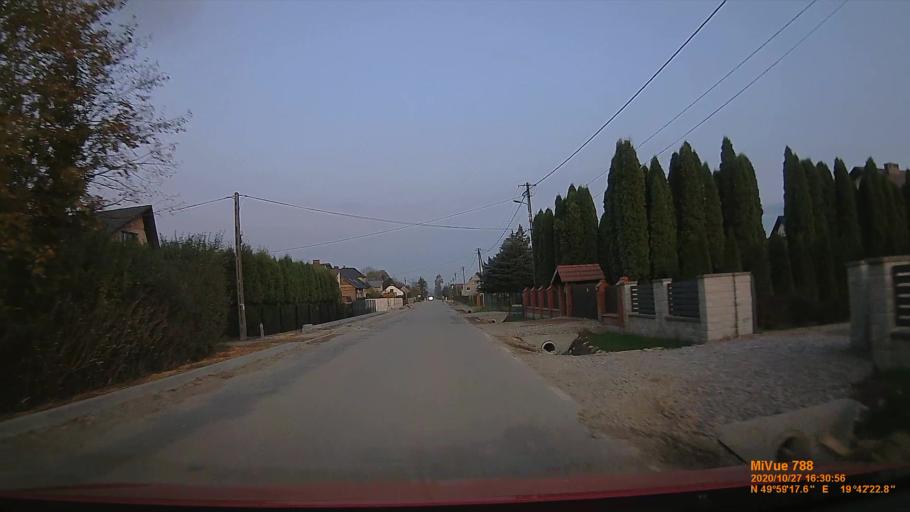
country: PL
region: Lesser Poland Voivodeship
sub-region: Powiat krakowski
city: Wolowice
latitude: 49.9882
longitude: 19.7065
